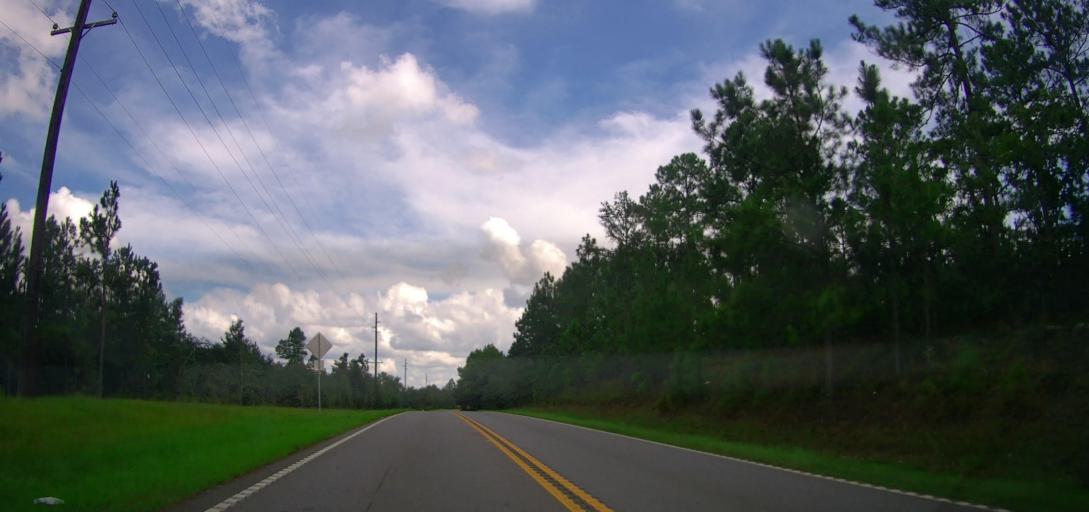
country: US
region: Georgia
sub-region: Talbot County
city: Talbotton
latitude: 32.6111
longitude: -84.4828
